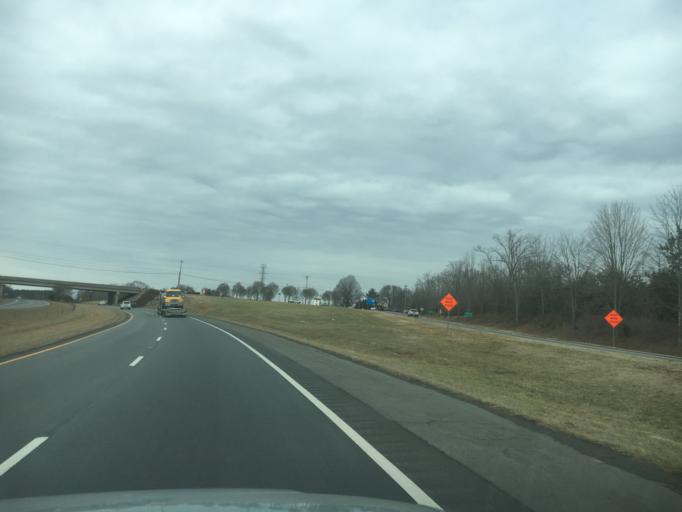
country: US
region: North Carolina
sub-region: Catawba County
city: Maiden
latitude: 35.5258
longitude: -81.2219
